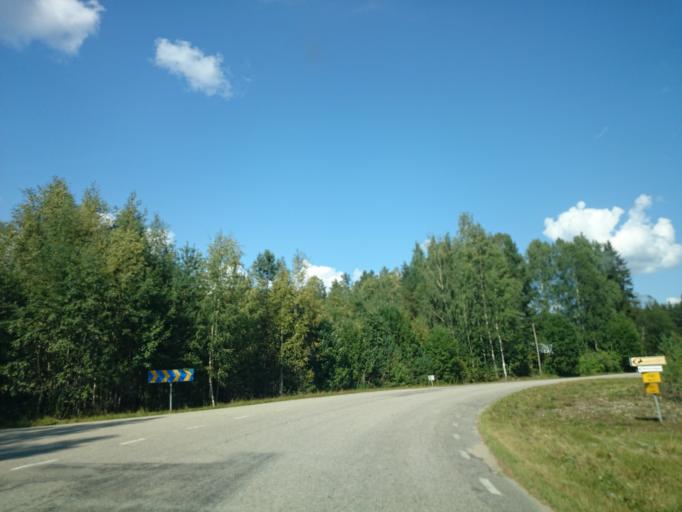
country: SE
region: Gaevleborg
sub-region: Ljusdals Kommun
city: Jaervsoe
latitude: 61.7764
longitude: 16.2119
